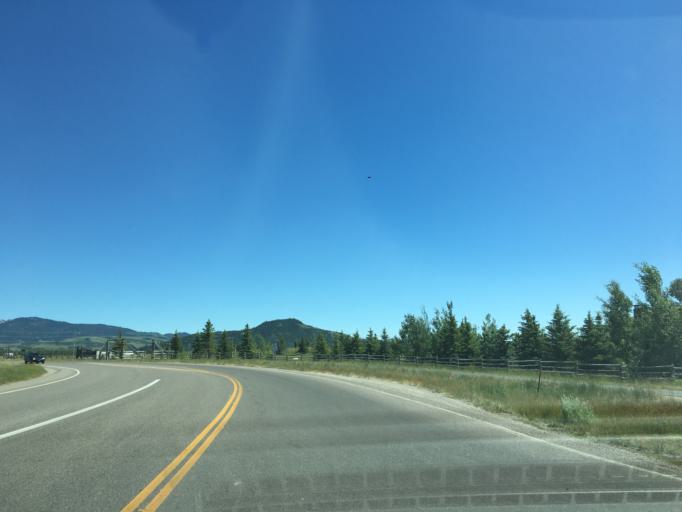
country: US
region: Wyoming
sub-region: Teton County
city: Moose Wilson Road
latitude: 43.5851
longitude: -110.8258
